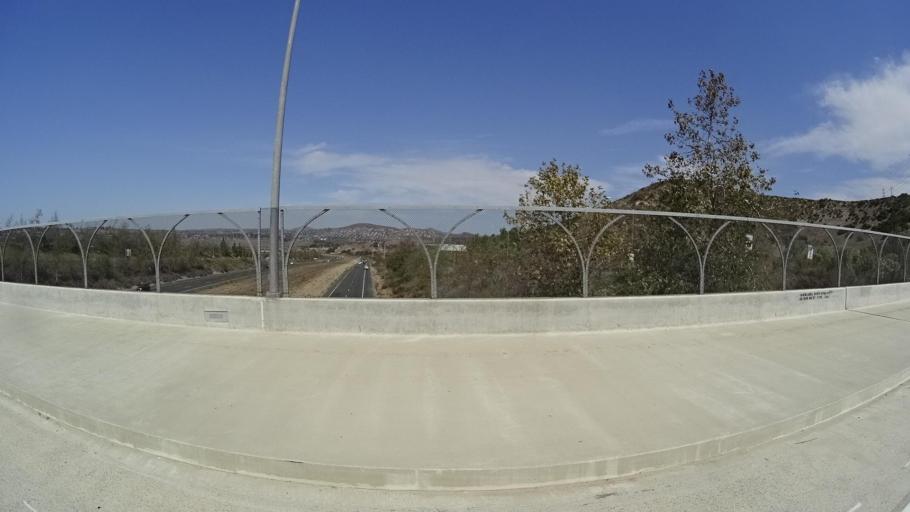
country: US
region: California
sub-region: San Diego County
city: La Presa
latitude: 32.6707
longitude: -116.9846
